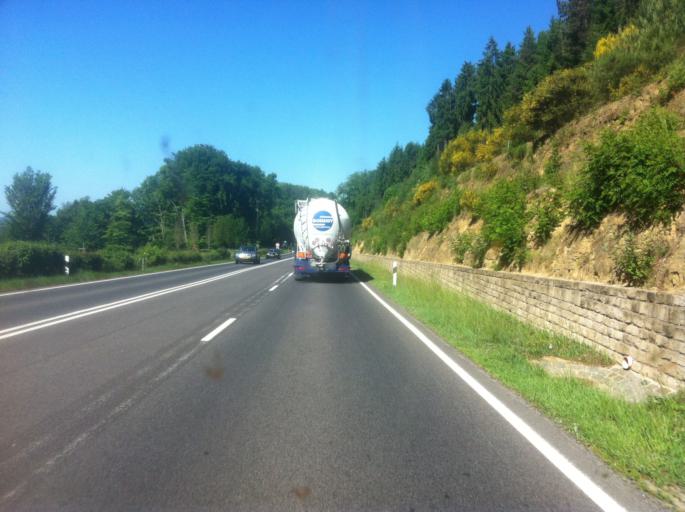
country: LU
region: Grevenmacher
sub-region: Canton d'Echternach
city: Consdorf
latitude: 49.7453
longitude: 6.3043
